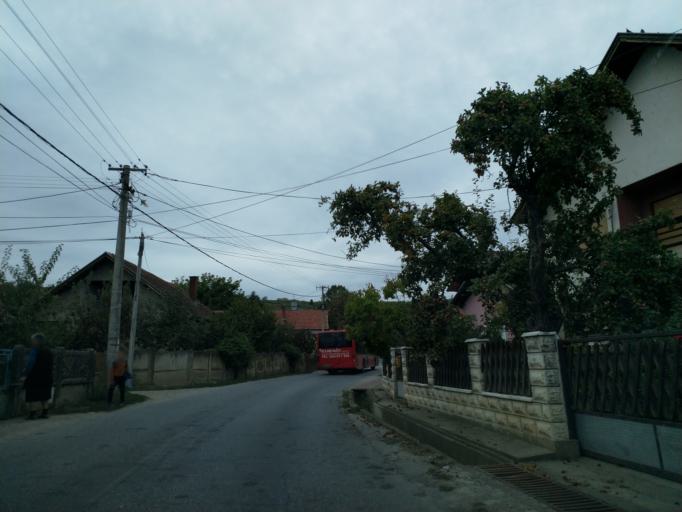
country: RS
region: Central Serbia
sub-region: Pomoravski Okrug
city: Paracin
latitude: 43.8354
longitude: 21.3232
